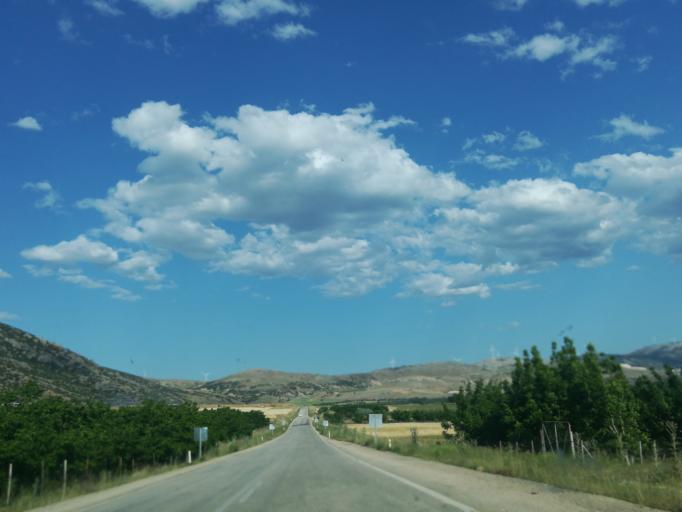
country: TR
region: Afyonkarahisar
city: Dinar
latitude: 38.1008
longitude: 30.1334
